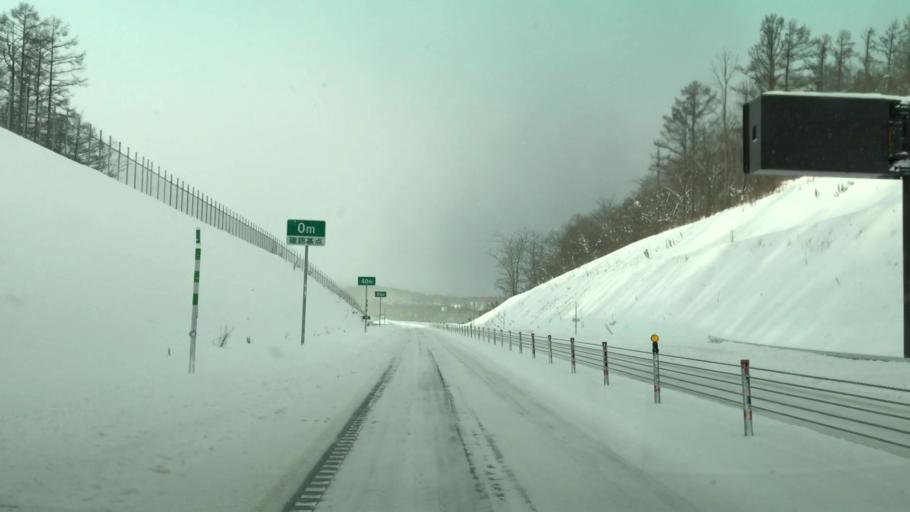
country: JP
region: Hokkaido
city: Yoichi
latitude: 43.1955
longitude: 140.8849
